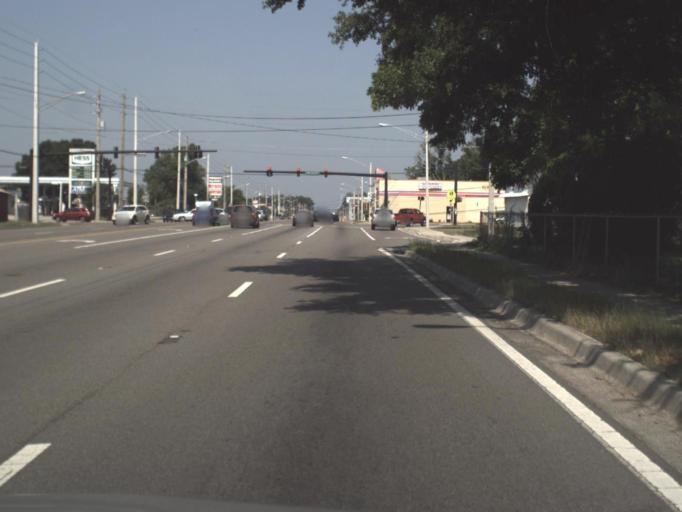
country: US
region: Florida
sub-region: Clay County
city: Bellair-Meadowbrook Terrace
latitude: 30.2485
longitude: -81.7379
